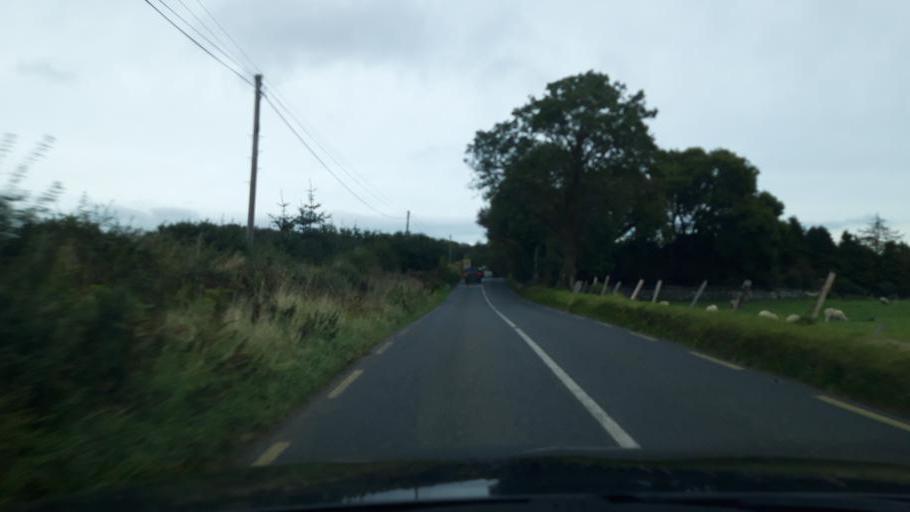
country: IE
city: Newtownmountkennedy
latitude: 53.1018
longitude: -6.1981
